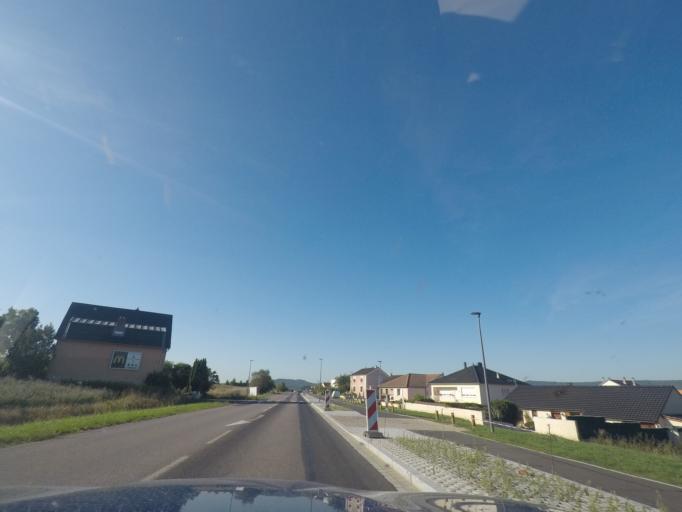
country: FR
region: Lorraine
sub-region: Departement de la Moselle
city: Hettange-Grande
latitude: 49.4183
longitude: 6.1593
